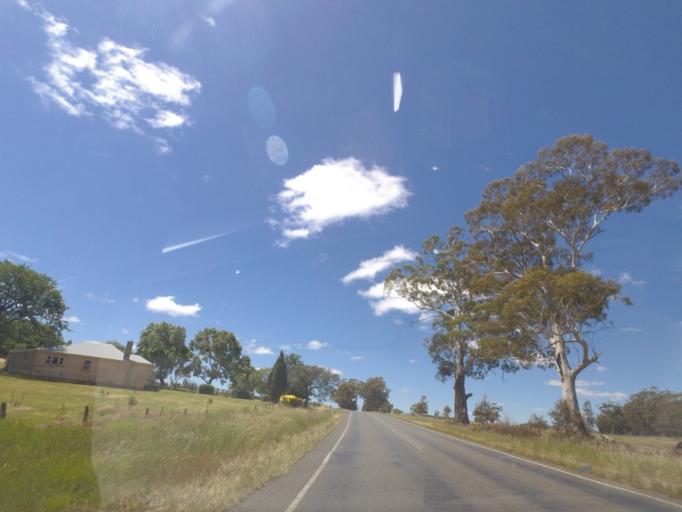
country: AU
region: Victoria
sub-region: Mount Alexander
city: Castlemaine
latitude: -37.3138
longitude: 144.2260
